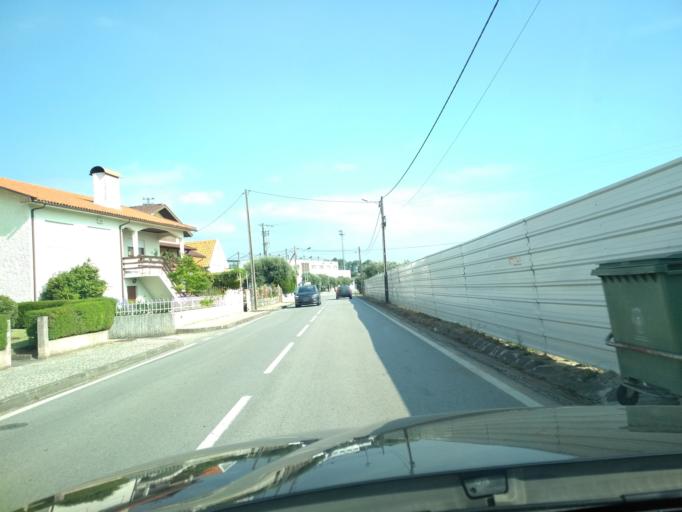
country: PT
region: Aveiro
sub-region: Mealhada
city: Mealhada
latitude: 40.3754
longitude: -8.4571
